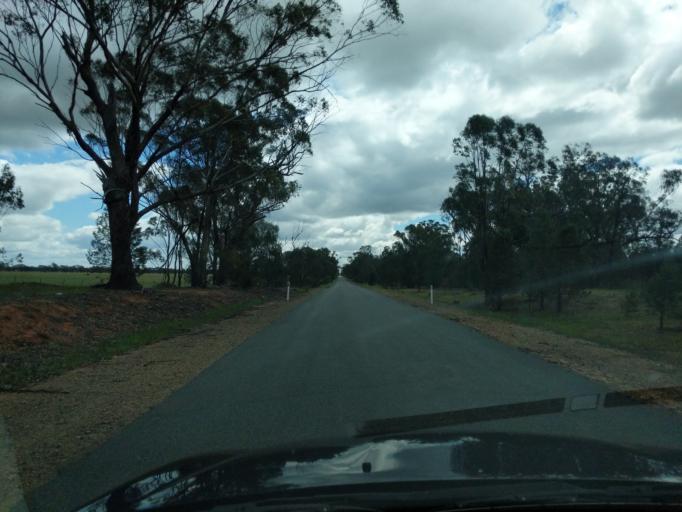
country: AU
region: New South Wales
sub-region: Coolamon
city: Coolamon
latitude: -34.9400
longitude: 146.9712
